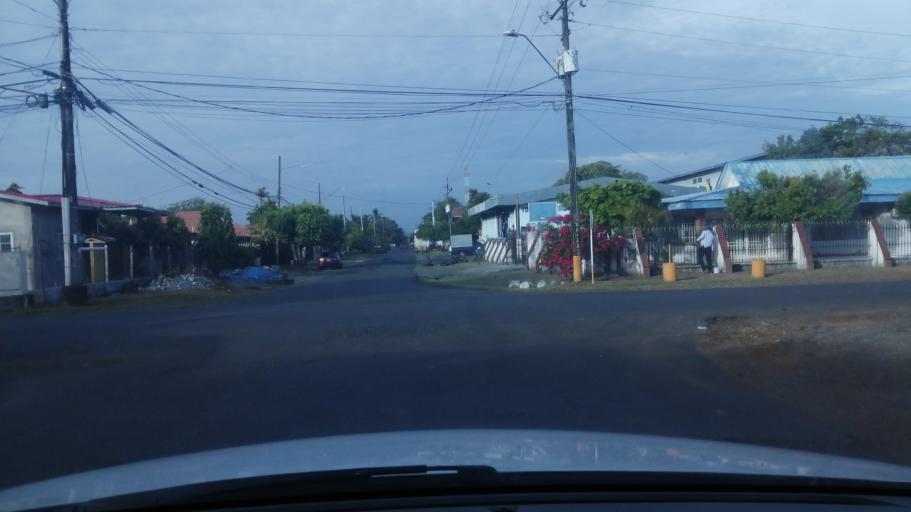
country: PA
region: Chiriqui
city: David
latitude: 8.4412
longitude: -82.4332
